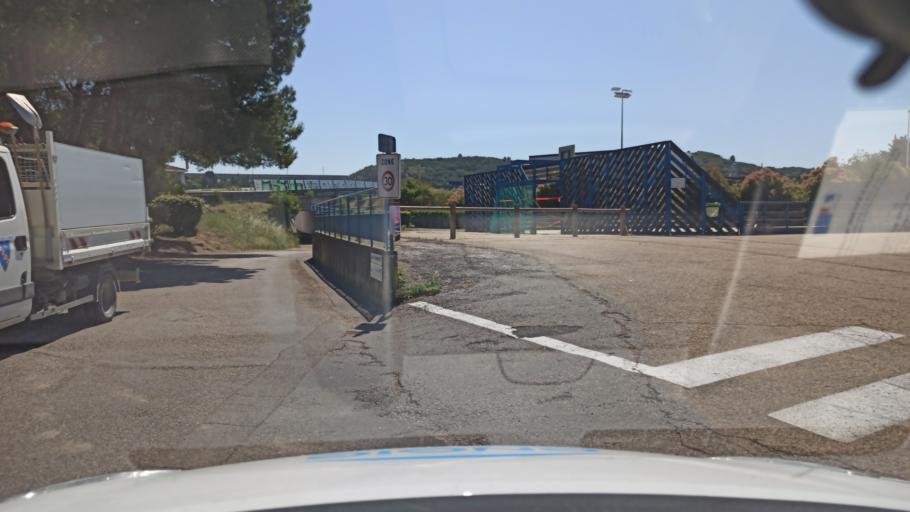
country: FR
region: Languedoc-Roussillon
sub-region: Departement du Gard
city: Les Angles
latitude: 43.9596
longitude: 4.7335
